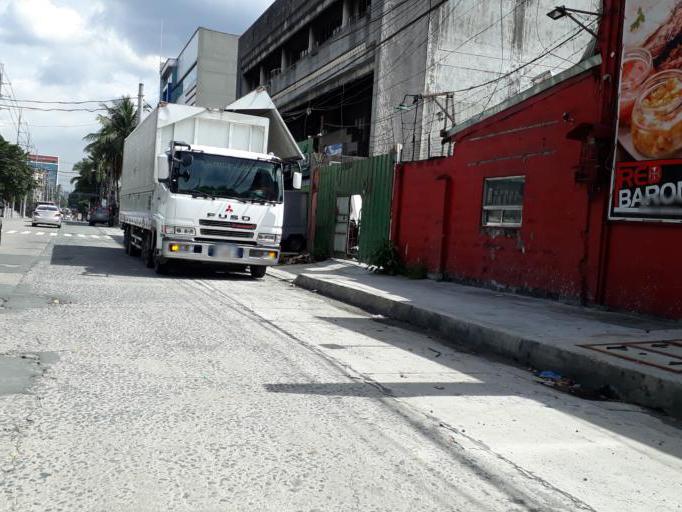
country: PH
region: Calabarzon
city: Del Monte
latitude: 14.6288
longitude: 121.0002
